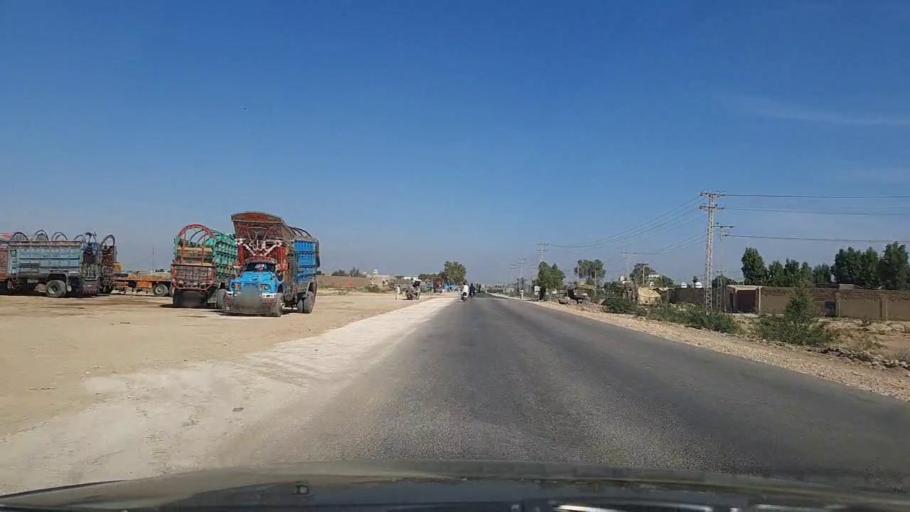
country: PK
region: Sindh
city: Kotri
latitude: 25.3376
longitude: 68.2480
